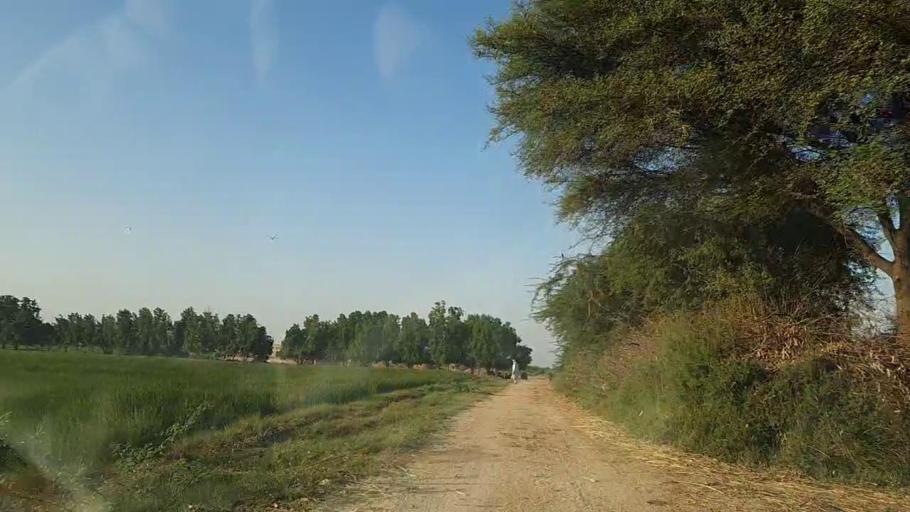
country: PK
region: Sindh
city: Jati
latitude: 24.4181
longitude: 68.1706
